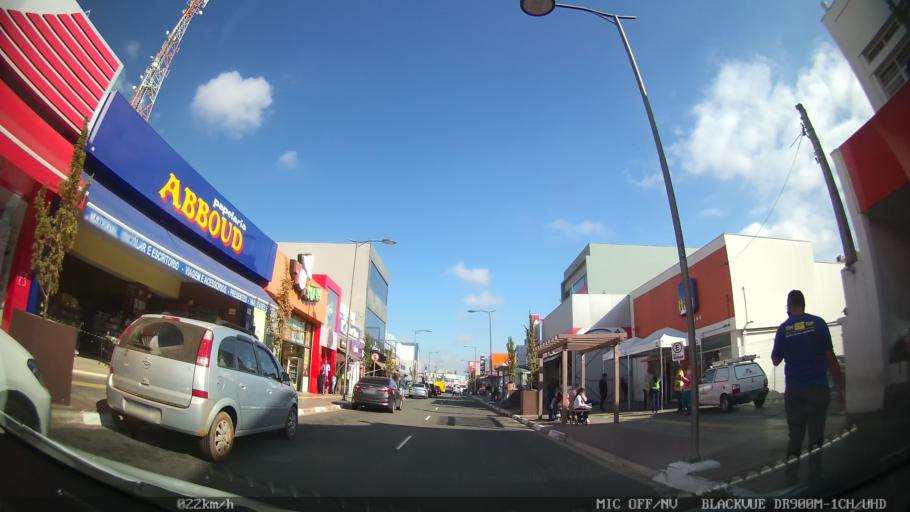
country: BR
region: Sao Paulo
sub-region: Hortolandia
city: Hortolandia
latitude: -22.8642
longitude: -47.2158
